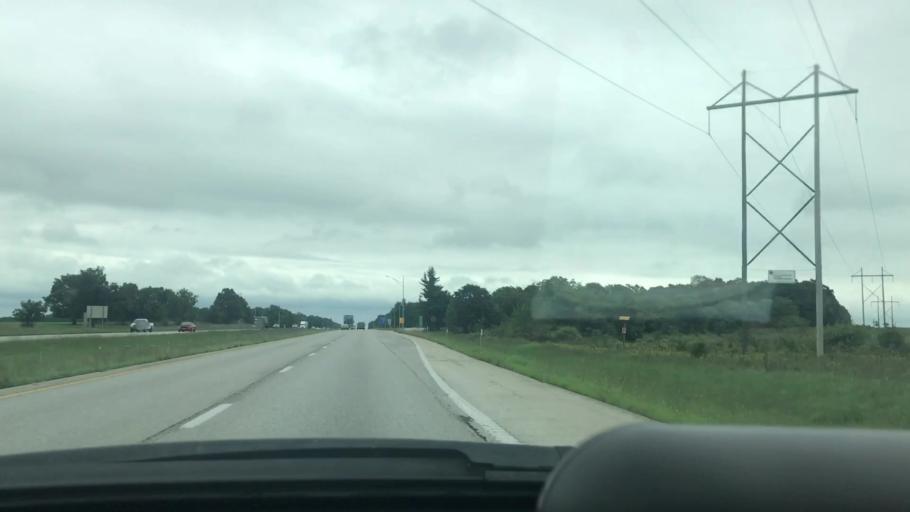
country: US
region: Missouri
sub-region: Lawrence County
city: Mount Vernon
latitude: 37.1366
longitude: -93.7266
